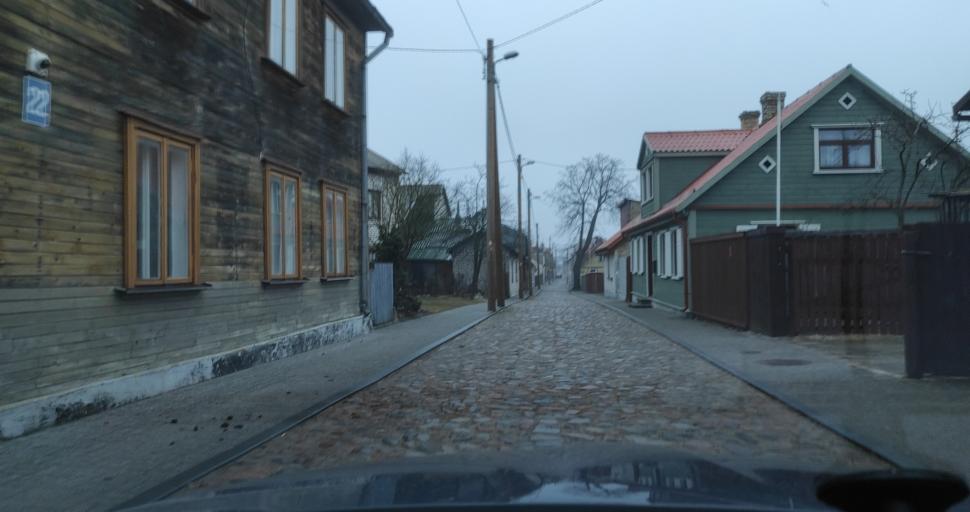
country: LV
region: Ventspils
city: Ventspils
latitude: 57.3915
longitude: 21.5451
